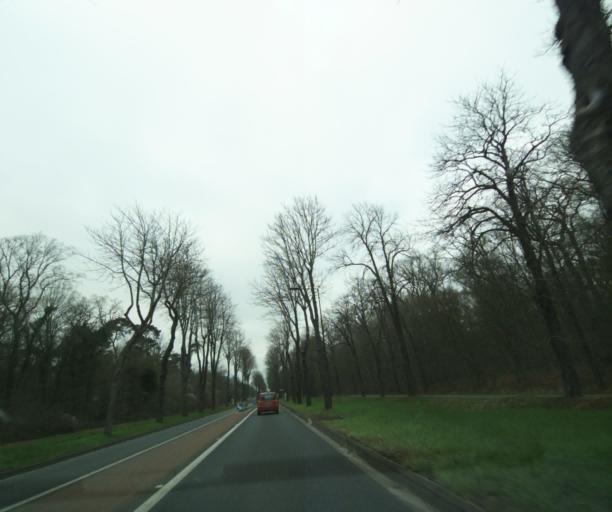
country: FR
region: Ile-de-France
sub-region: Departement des Yvelines
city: Poissy
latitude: 48.9187
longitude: 2.0616
